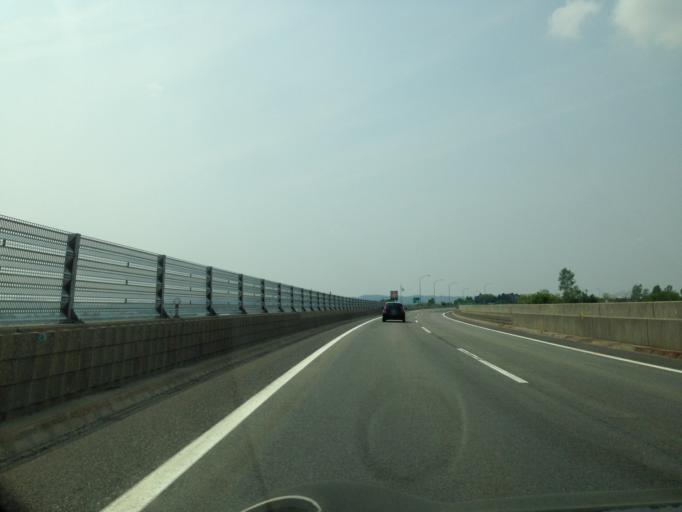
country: JP
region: Niigata
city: Gosen
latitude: 37.7602
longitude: 139.2176
